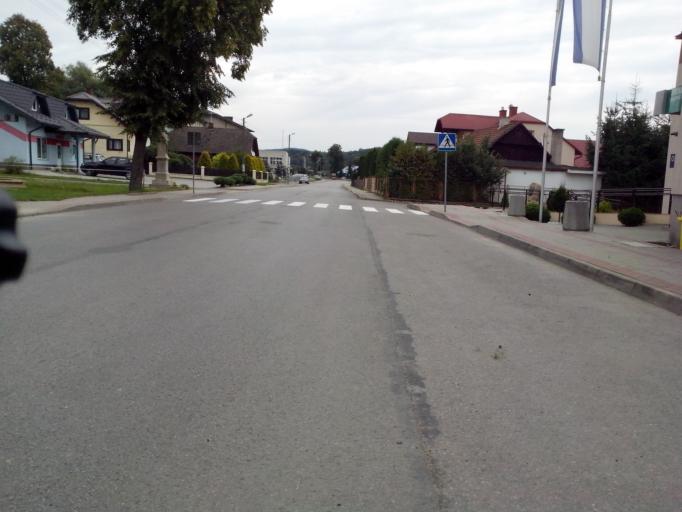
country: PL
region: Subcarpathian Voivodeship
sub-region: Powiat brzozowski
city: Jasienica Rosielna
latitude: 49.7505
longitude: 21.9390
